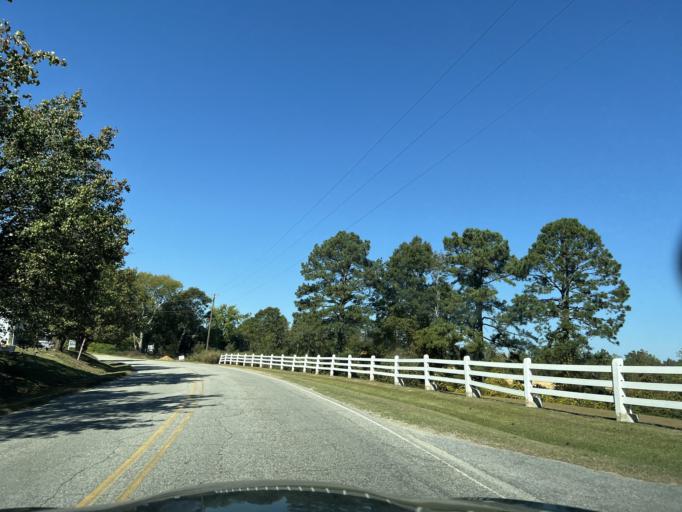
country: US
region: North Carolina
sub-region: Johnston County
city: Clayton
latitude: 35.6648
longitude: -78.4717
